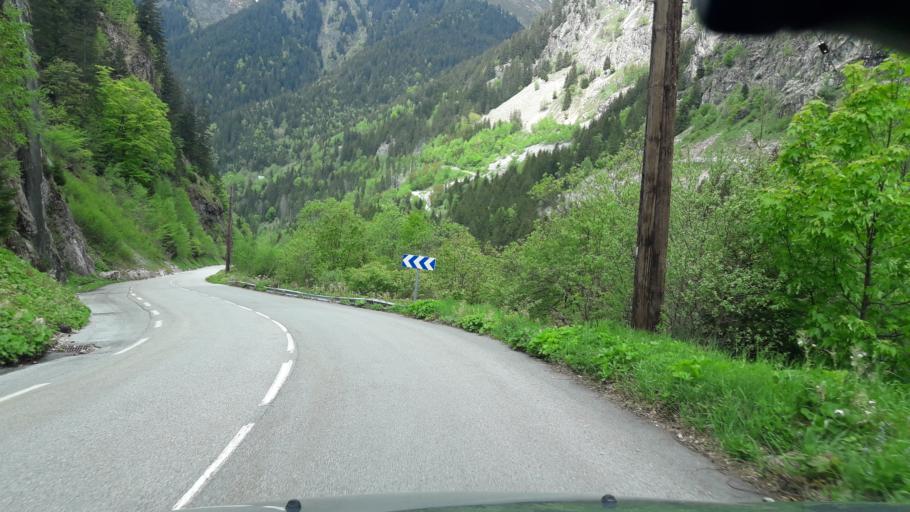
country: FR
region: Rhone-Alpes
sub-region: Departement de l'Isere
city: Theys
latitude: 45.2078
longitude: 6.0642
